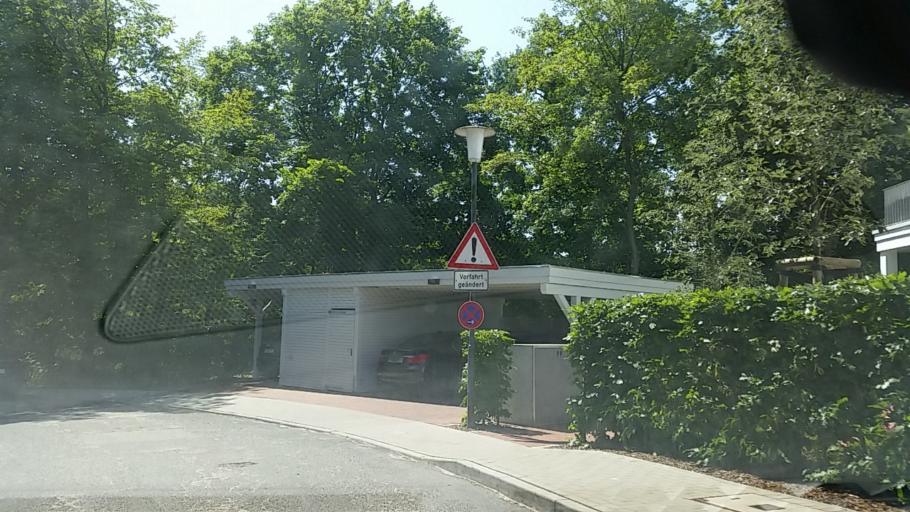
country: DE
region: Schleswig-Holstein
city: Wedel
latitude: 53.5667
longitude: 9.7824
